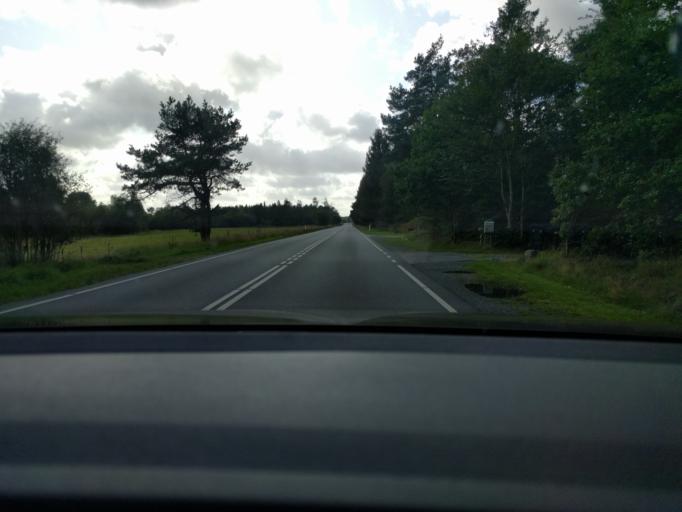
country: DK
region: Central Jutland
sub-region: Viborg Kommune
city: Bjerringbro
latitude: 56.2947
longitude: 9.6618
